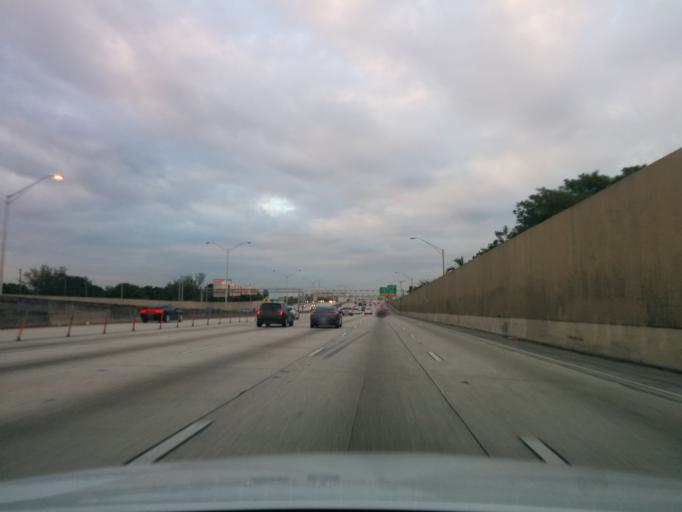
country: US
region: Florida
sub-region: Miami-Dade County
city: Allapattah
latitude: 25.8199
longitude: -80.2060
